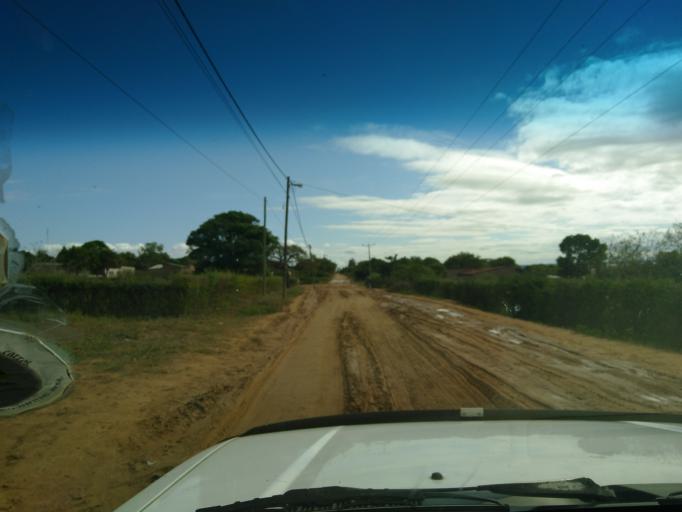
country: MZ
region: Maputo City
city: Maputo
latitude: -26.0012
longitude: 32.5431
